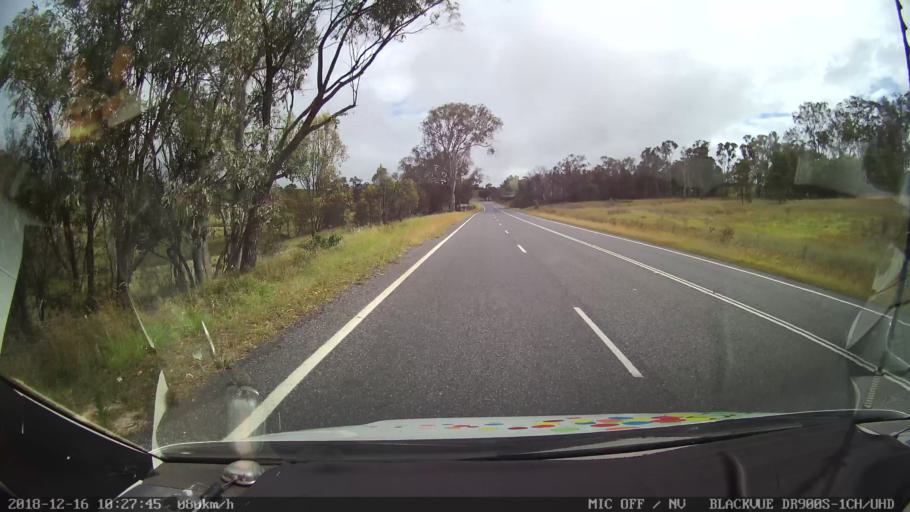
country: AU
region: New South Wales
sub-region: Tenterfield Municipality
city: Carrolls Creek
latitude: -29.1297
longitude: 151.9960
